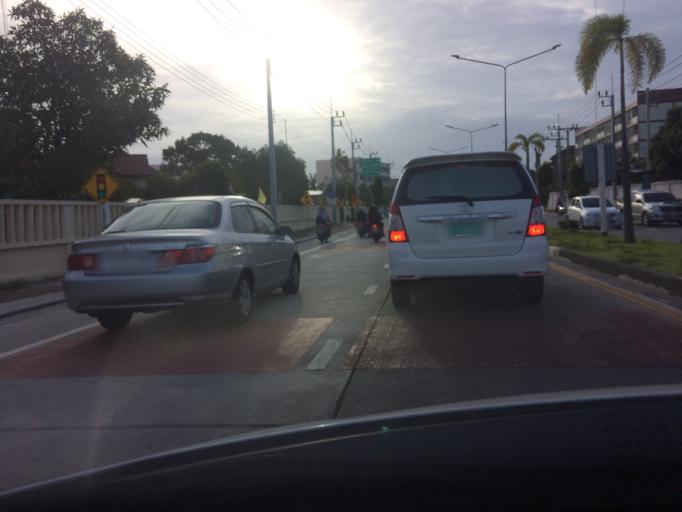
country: TH
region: Phuket
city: Ban Talat Nua
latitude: 7.8693
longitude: 98.3895
